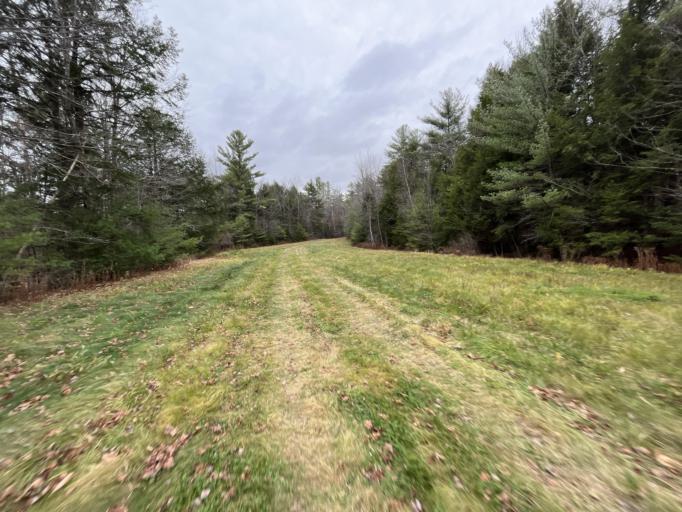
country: US
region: New Hampshire
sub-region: Merrimack County
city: New London
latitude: 43.4047
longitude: -71.9818
